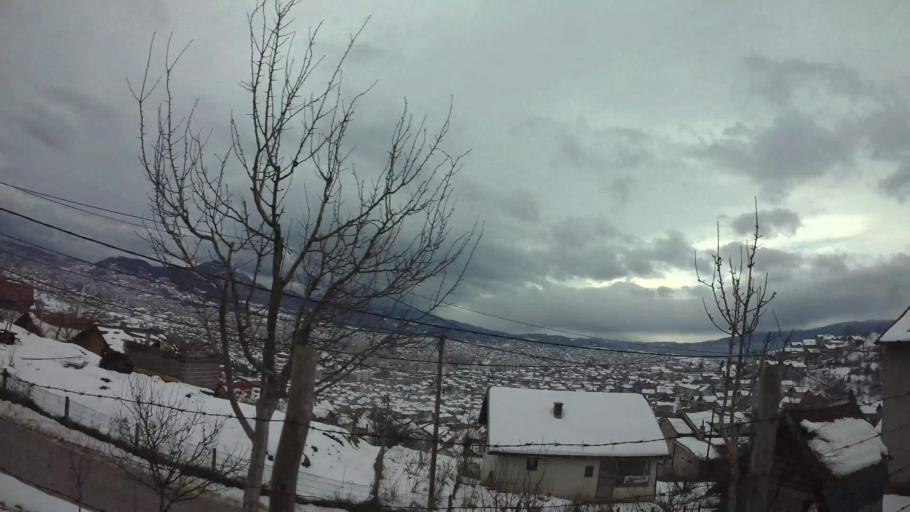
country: BA
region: Federation of Bosnia and Herzegovina
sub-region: Kanton Sarajevo
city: Sarajevo
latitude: 43.8640
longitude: 18.3559
